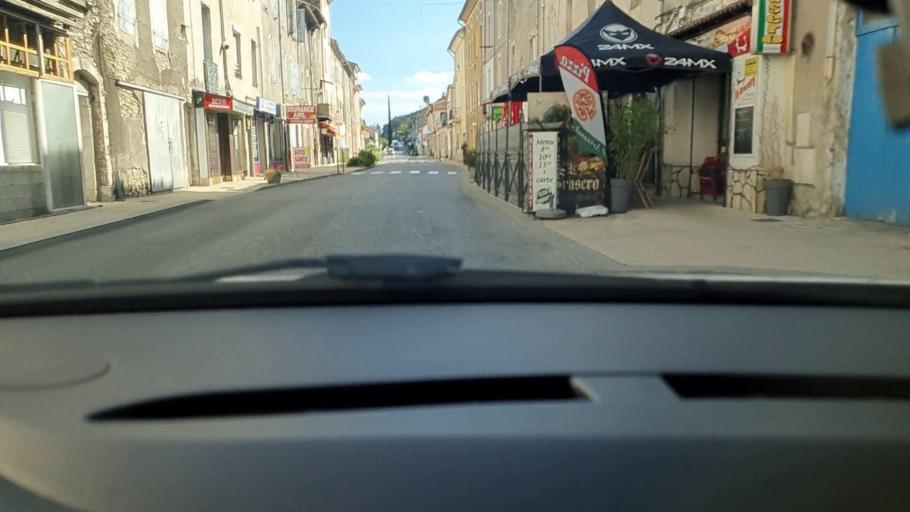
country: FR
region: Languedoc-Roussillon
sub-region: Departement du Gard
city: Saint-Ambroix
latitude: 44.2600
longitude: 4.1997
